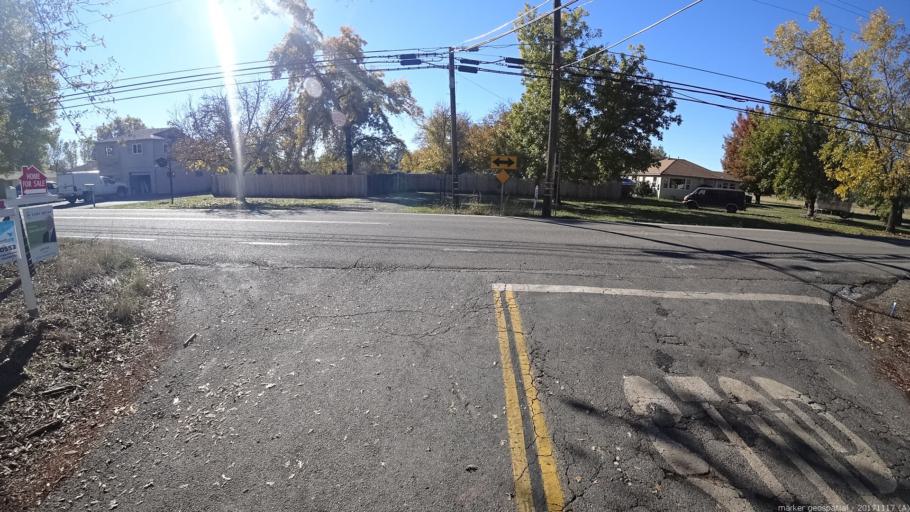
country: US
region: California
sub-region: Shasta County
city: Anderson
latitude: 40.4450
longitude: -122.2519
